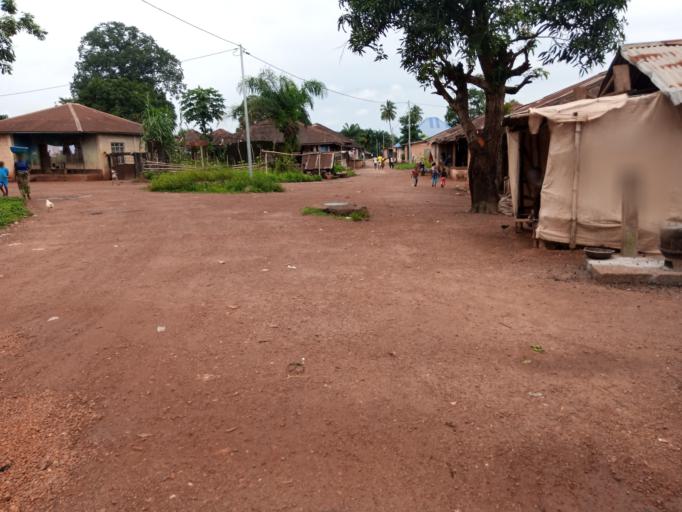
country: SL
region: Southern Province
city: Largo
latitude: 8.2044
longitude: -12.0616
